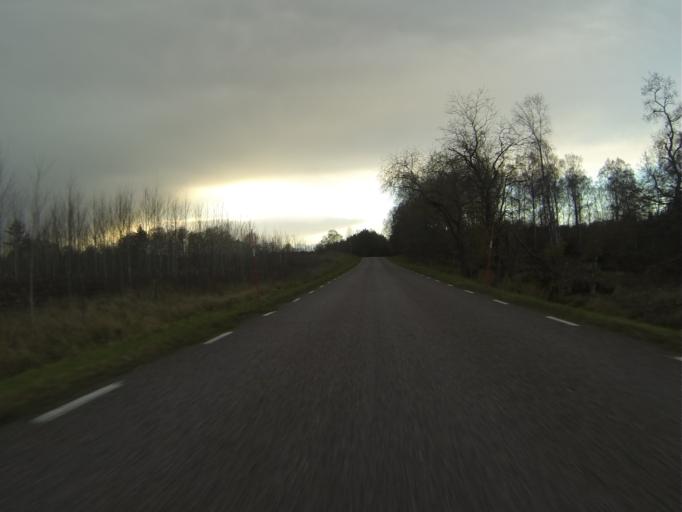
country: SE
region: Skane
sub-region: Lunds Kommun
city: Genarp
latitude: 55.5812
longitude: 13.3990
